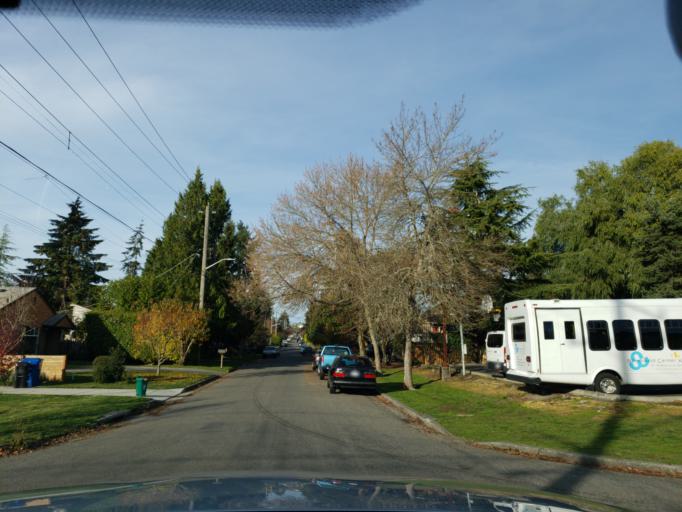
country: US
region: Washington
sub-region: King County
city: Shoreline
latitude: 47.6978
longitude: -122.3567
